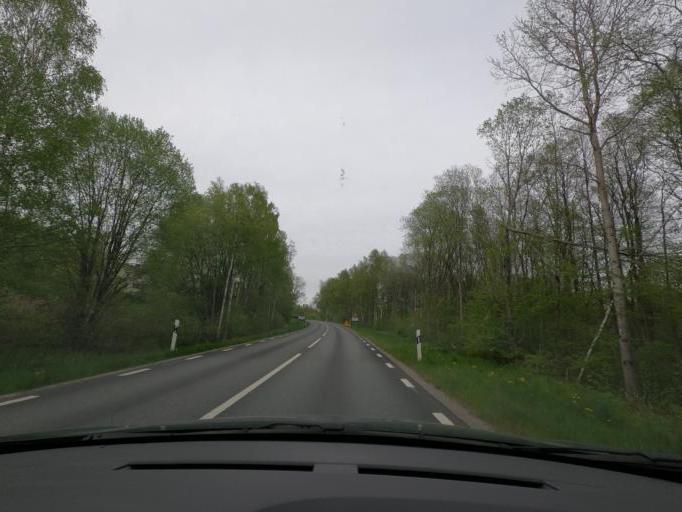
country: SE
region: Joenkoeping
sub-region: Varnamo Kommun
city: Bredaryd
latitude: 57.2171
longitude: 13.7766
